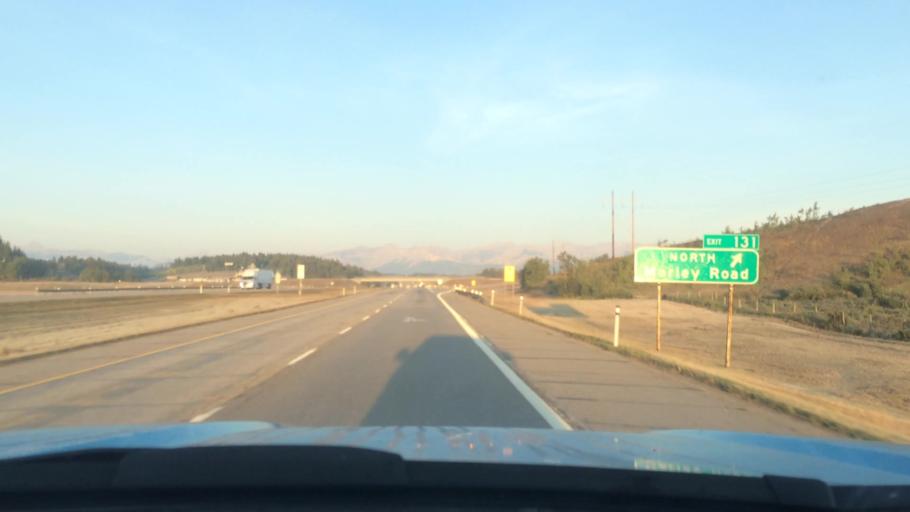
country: CA
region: Alberta
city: Cochrane
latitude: 51.1488
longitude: -114.8336
